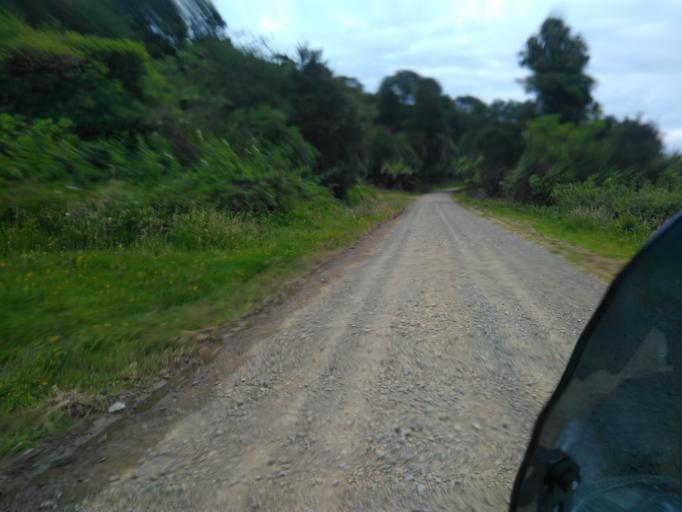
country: NZ
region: Bay of Plenty
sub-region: Opotiki District
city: Opotiki
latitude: -38.0269
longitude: 177.4396
